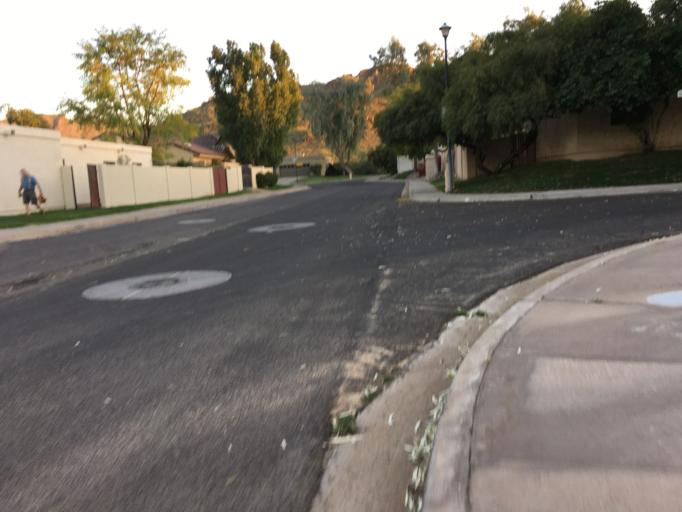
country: US
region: Arizona
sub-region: Maricopa County
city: Paradise Valley
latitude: 33.5693
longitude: -112.0077
